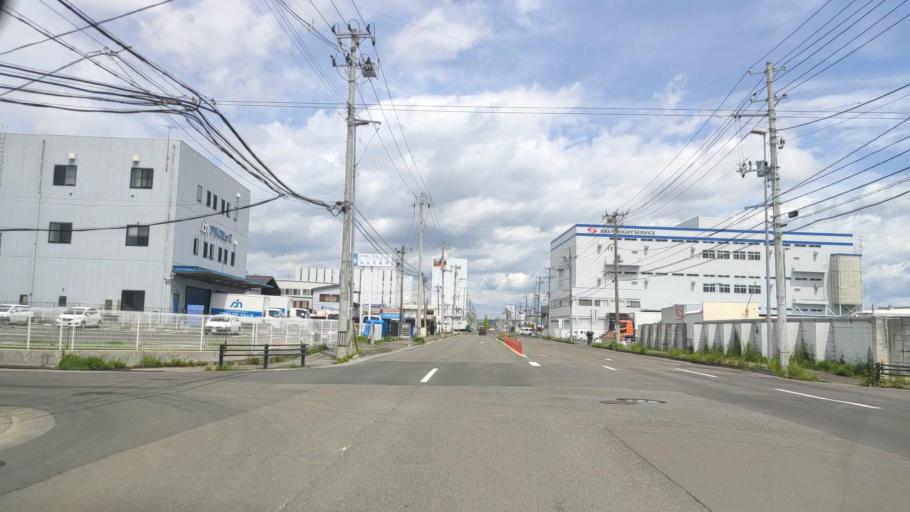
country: JP
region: Miyagi
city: Sendai-shi
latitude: 38.2640
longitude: 140.9432
